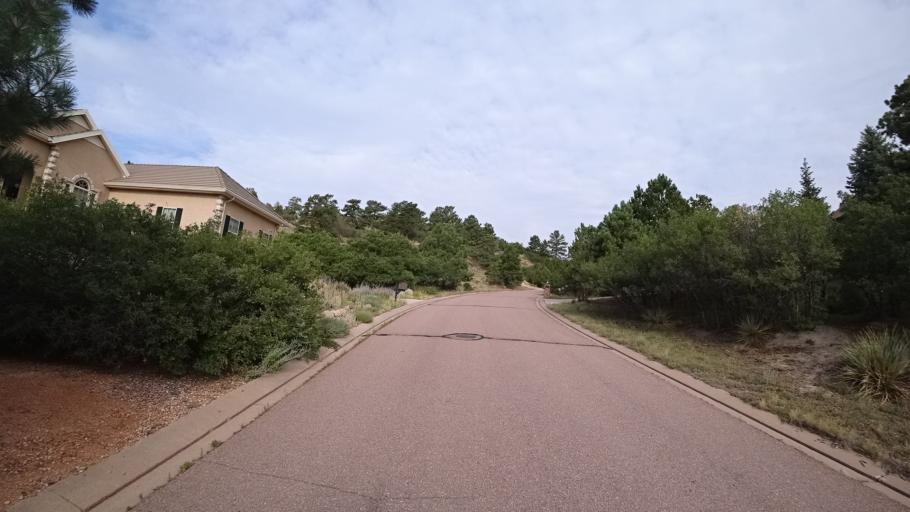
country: US
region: Colorado
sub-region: El Paso County
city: Air Force Academy
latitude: 38.9343
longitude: -104.8455
